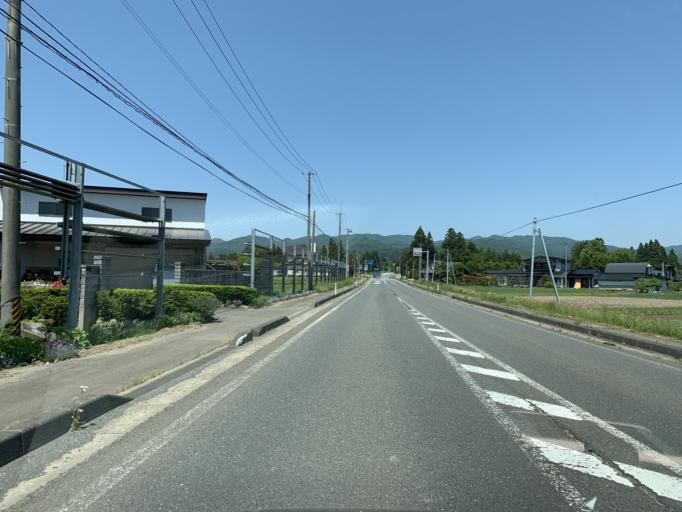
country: JP
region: Iwate
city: Kitakami
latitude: 39.2967
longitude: 140.9815
